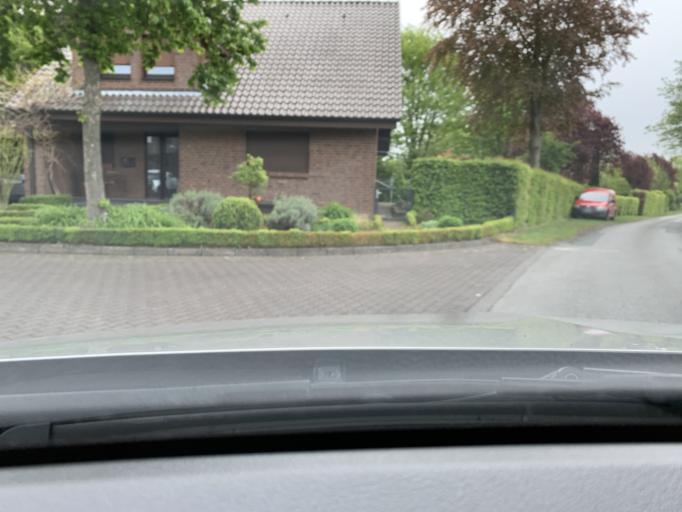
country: DE
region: North Rhine-Westphalia
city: Rietberg
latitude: 51.8000
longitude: 8.3786
